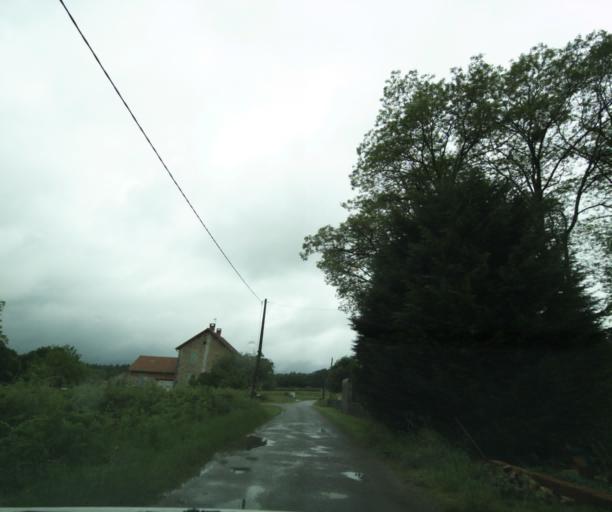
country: FR
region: Bourgogne
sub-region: Departement de Saone-et-Loire
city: Ciry-le-Noble
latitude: 46.5245
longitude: 4.3030
